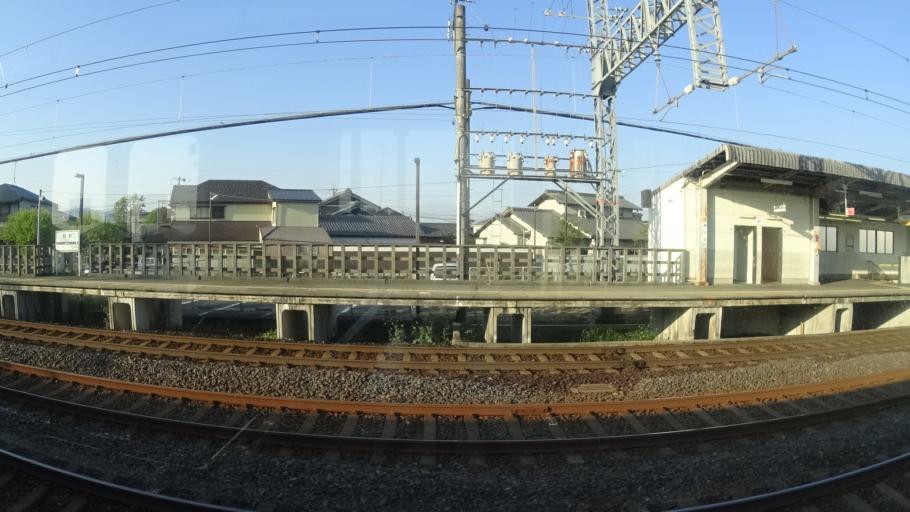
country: JP
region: Mie
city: Ise
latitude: 34.5214
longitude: 136.6691
